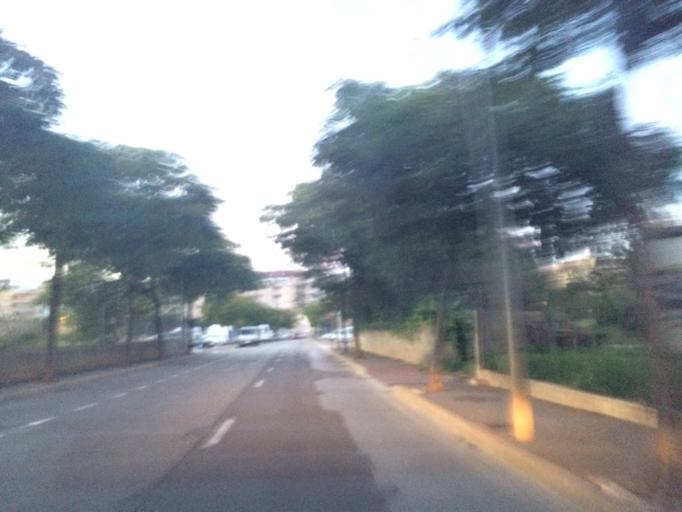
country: ES
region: Valencia
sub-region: Provincia de Alicante
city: Denia
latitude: 38.8342
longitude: 0.1104
